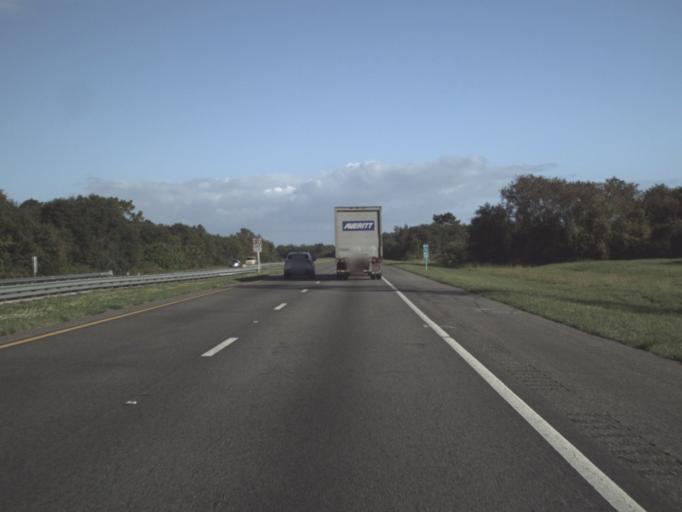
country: US
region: Florida
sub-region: Brevard County
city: June Park
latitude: 27.8516
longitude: -81.0078
